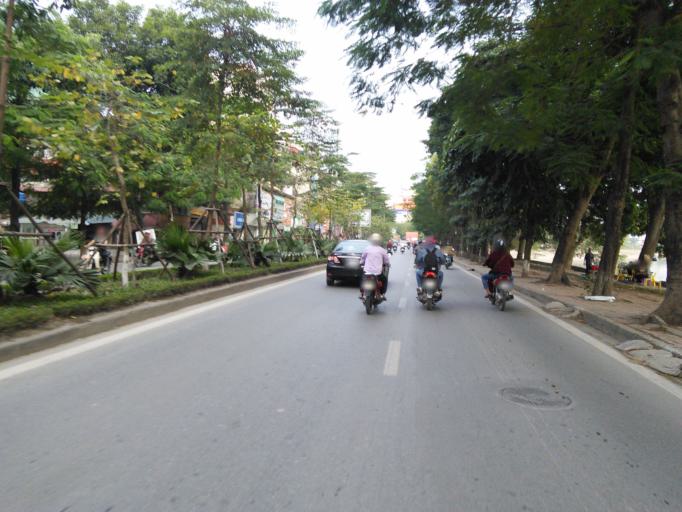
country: VN
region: Ha Noi
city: Van Dien
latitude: 20.9710
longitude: 105.8370
